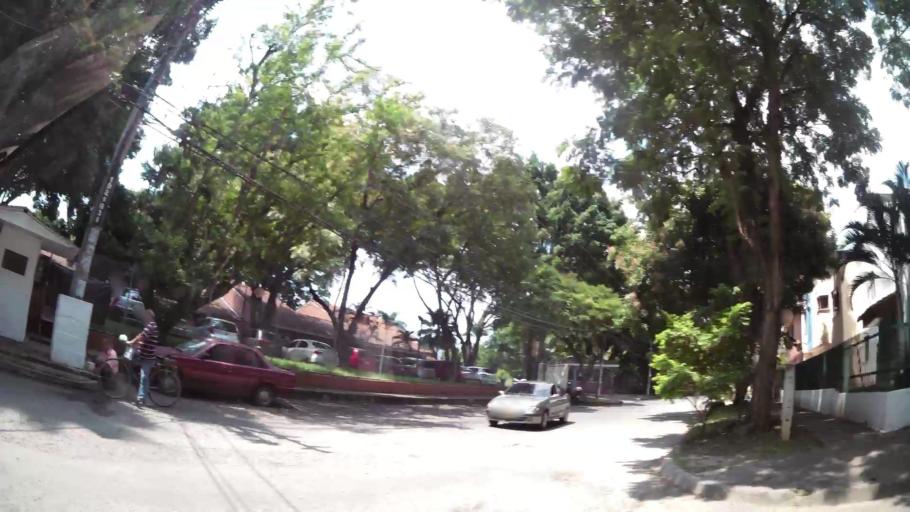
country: CO
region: Valle del Cauca
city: Cali
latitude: 3.3957
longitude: -76.5408
